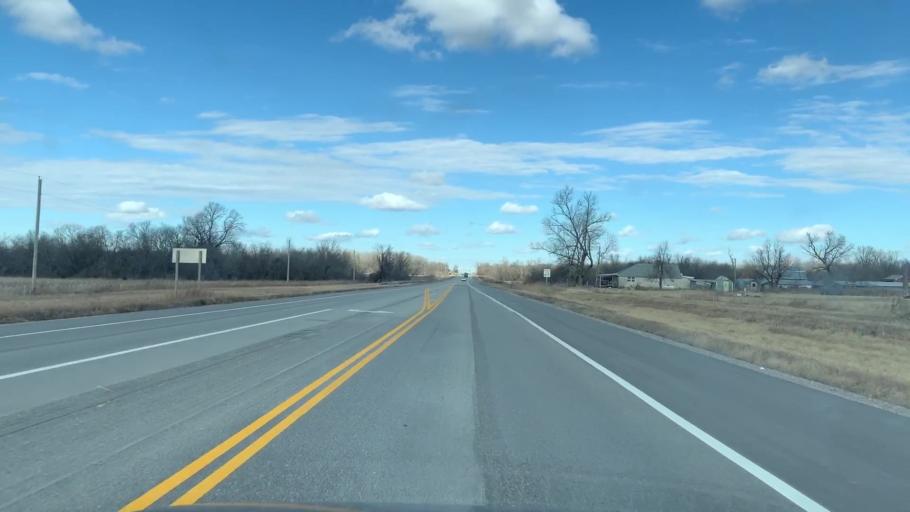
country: US
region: Kansas
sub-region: Cherokee County
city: Columbus
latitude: 37.3122
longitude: -94.8322
